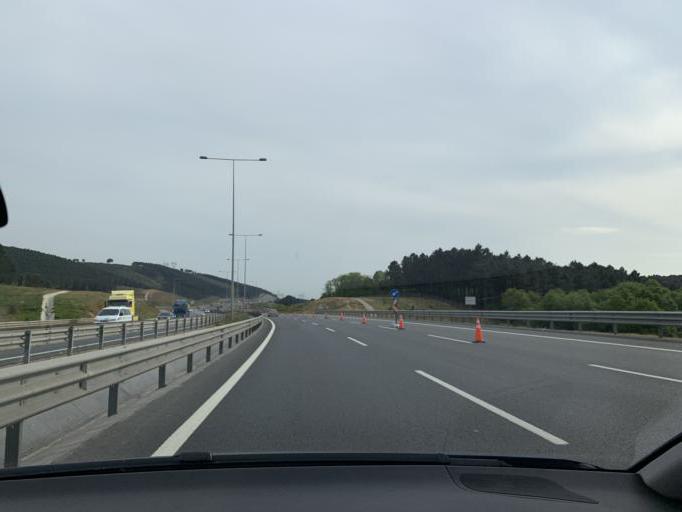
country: TR
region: Istanbul
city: Sultanbeyli
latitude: 40.9698
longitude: 29.3225
